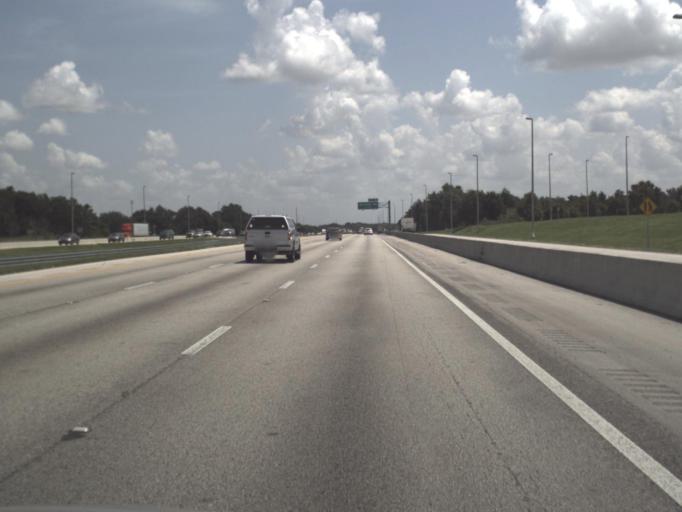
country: US
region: Florida
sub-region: Hillsborough County
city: Seffner
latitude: 28.0161
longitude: -82.2674
